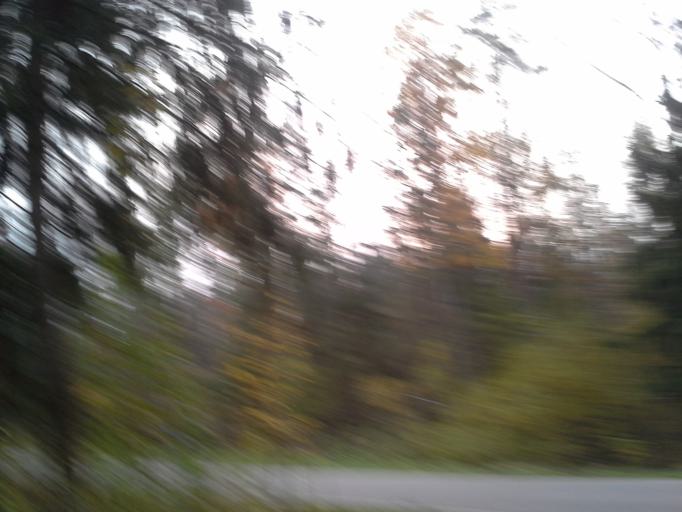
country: RU
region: Moskovskaya
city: Nazar'yevo
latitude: 55.6949
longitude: 36.9779
